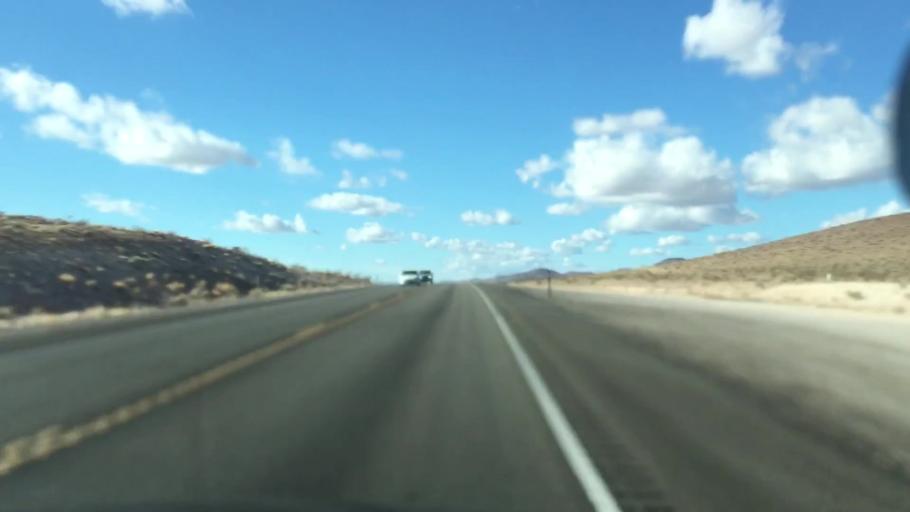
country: US
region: Nevada
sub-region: Nye County
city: Pahrump
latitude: 36.6116
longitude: -116.2729
